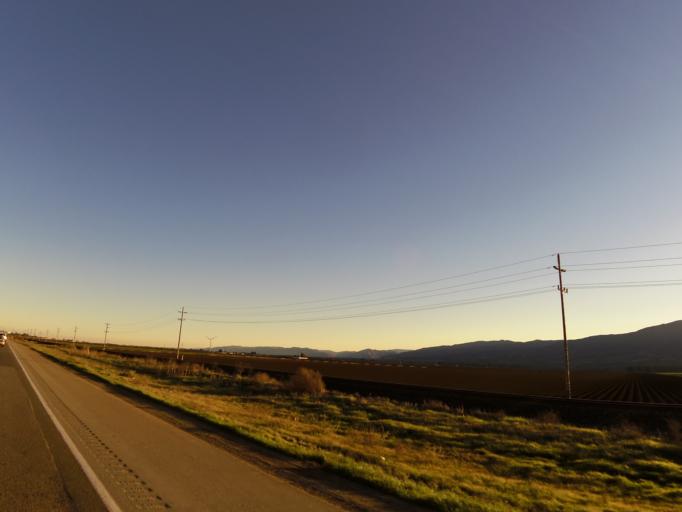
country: US
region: California
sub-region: Monterey County
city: Soledad
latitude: 36.4444
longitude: -121.3569
